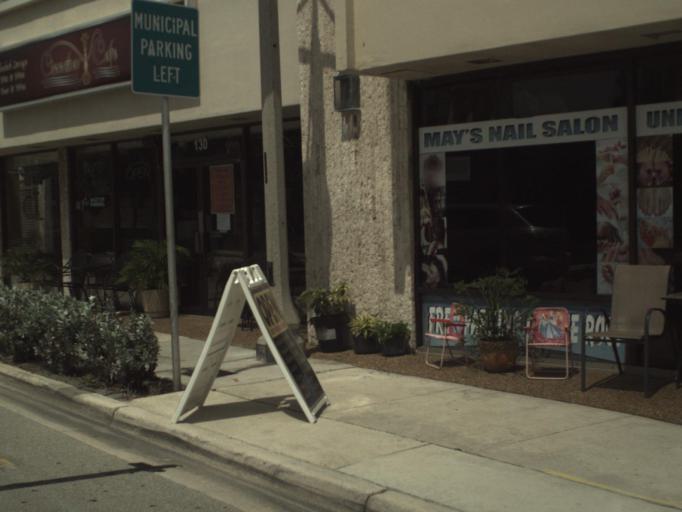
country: US
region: Florida
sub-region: Broward County
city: Terra Mar
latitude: 26.2345
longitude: -80.0907
